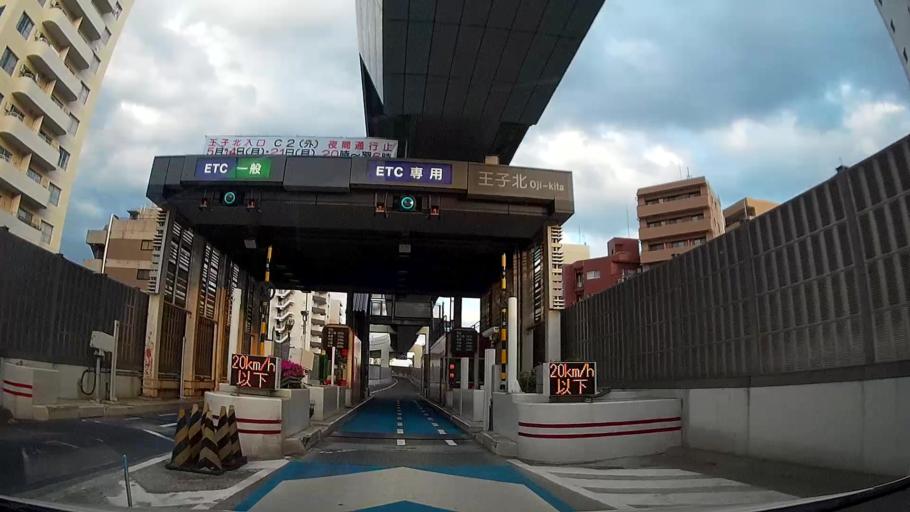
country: JP
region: Saitama
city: Kawaguchi
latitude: 35.7566
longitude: 139.7407
